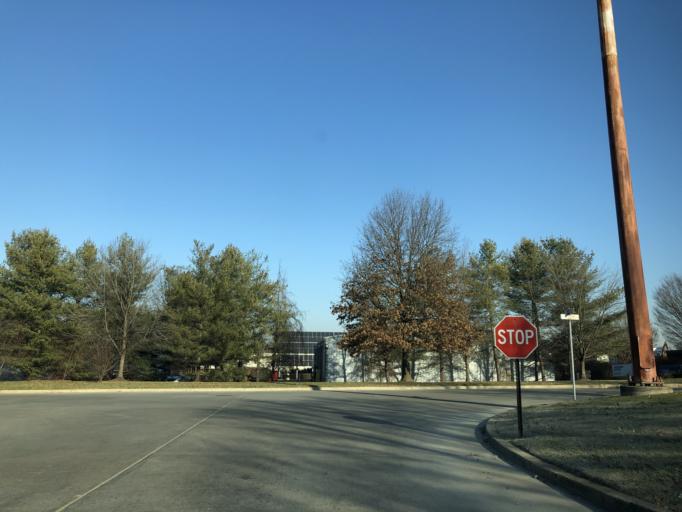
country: US
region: Pennsylvania
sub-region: Chester County
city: Downingtown
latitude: 39.9991
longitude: -75.6986
